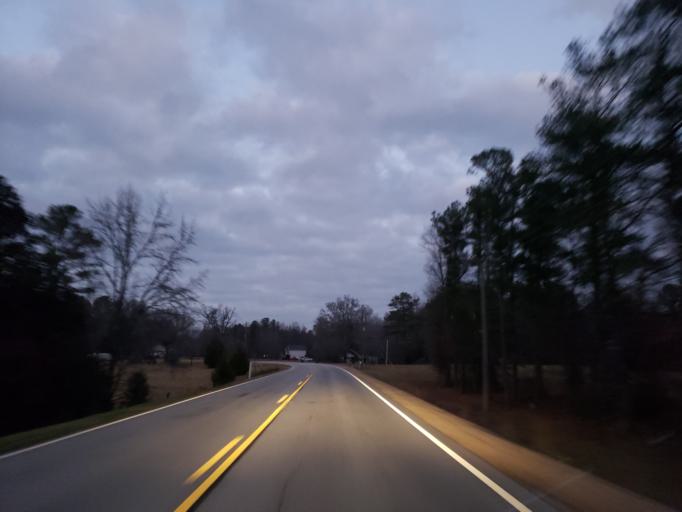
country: US
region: Georgia
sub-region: Carroll County
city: Temple
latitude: 33.7919
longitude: -85.0611
